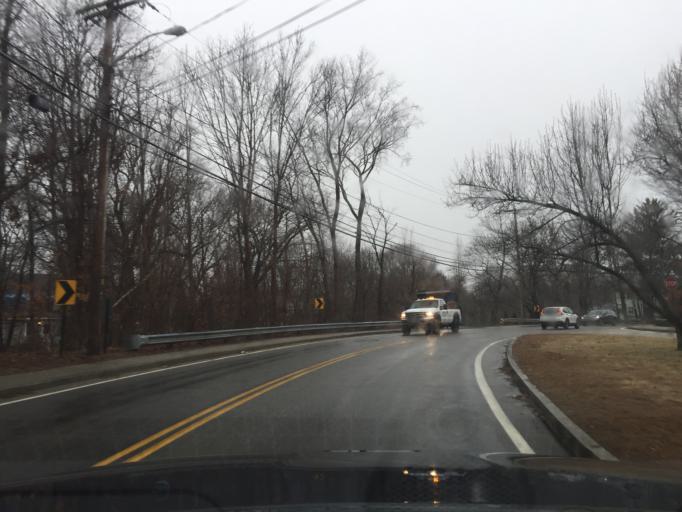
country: US
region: Massachusetts
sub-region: Plymouth County
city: Plymouth
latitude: 41.9452
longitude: -70.6612
